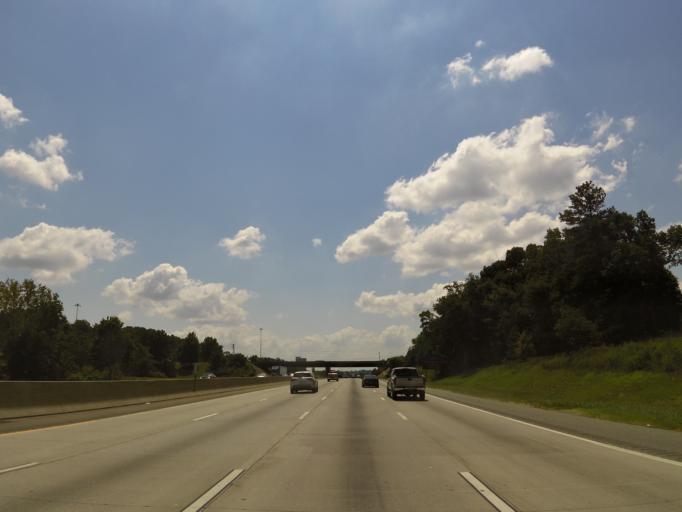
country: US
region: North Carolina
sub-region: Cabarrus County
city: Harrisburg
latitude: 35.3344
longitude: -80.7436
